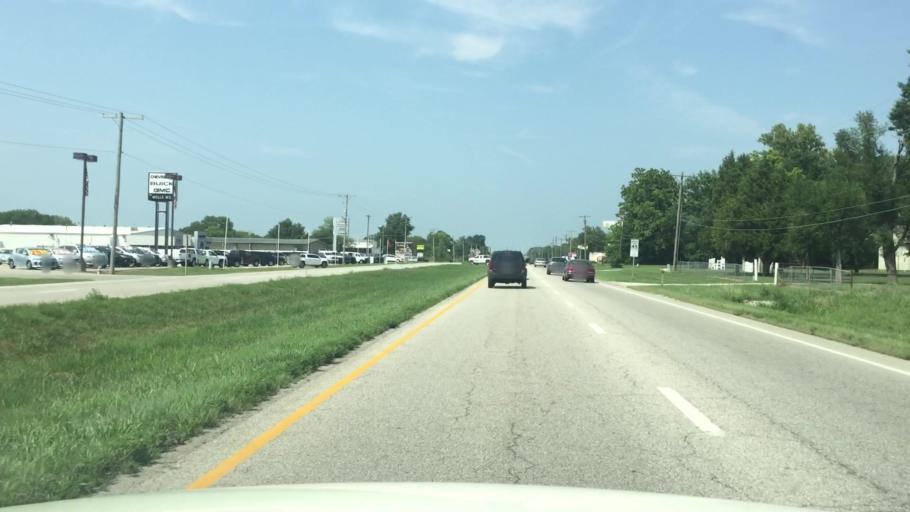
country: US
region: Kansas
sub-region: Crawford County
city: Frontenac
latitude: 37.4581
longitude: -94.7051
